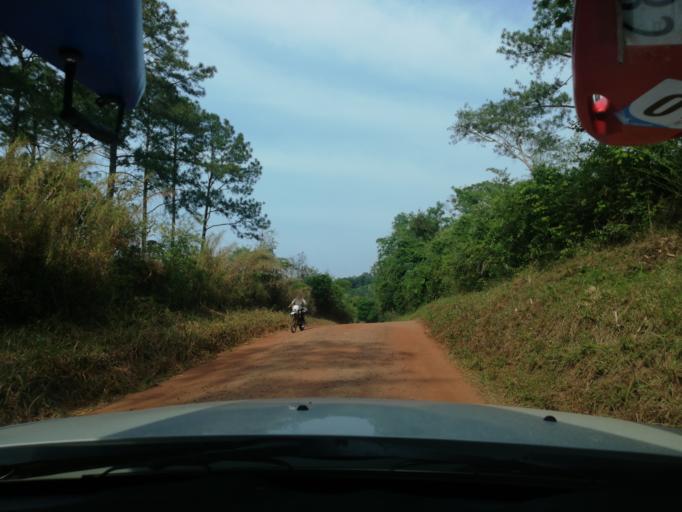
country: AR
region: Misiones
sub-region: Departamento de San Ignacio
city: San Ignacio
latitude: -27.2934
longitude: -55.5651
